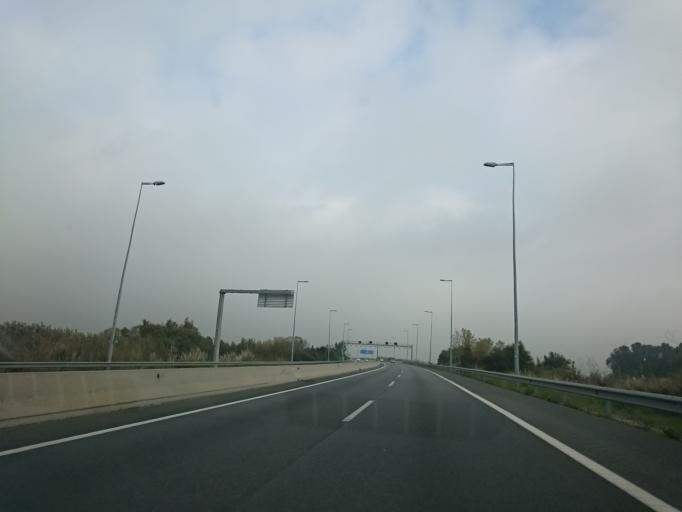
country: ES
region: Catalonia
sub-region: Provincia de Barcelona
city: Viladecans
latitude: 41.2831
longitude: 2.0528
